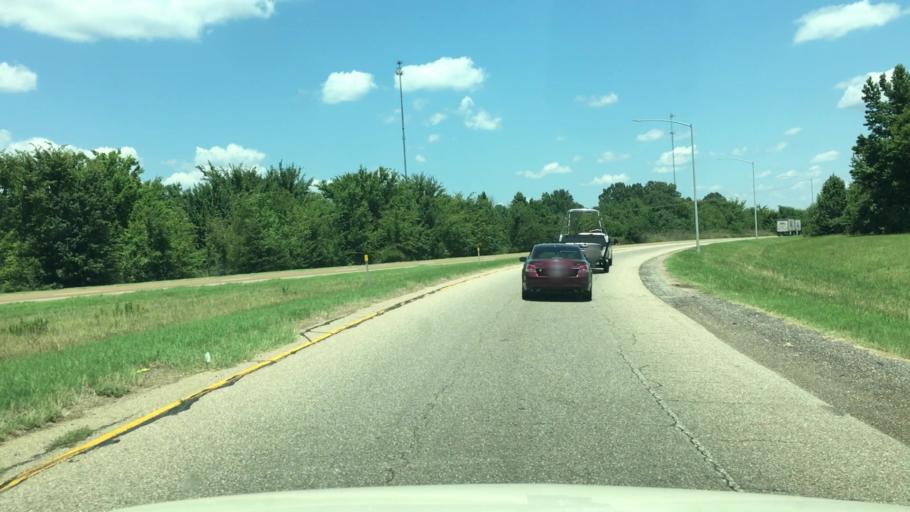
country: US
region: Arkansas
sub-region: Nevada County
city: Prescott
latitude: 33.8124
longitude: -93.4200
